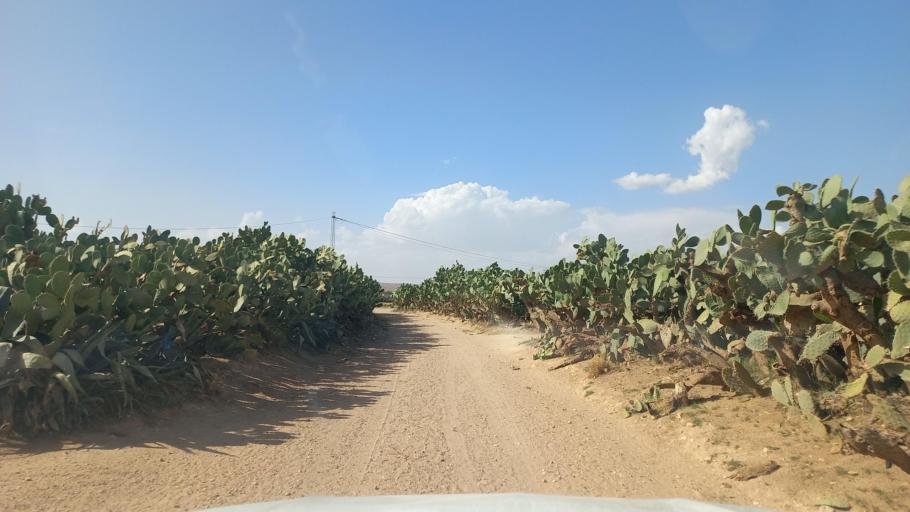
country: TN
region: Al Qasrayn
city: Sbiba
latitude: 35.3161
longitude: 9.0297
